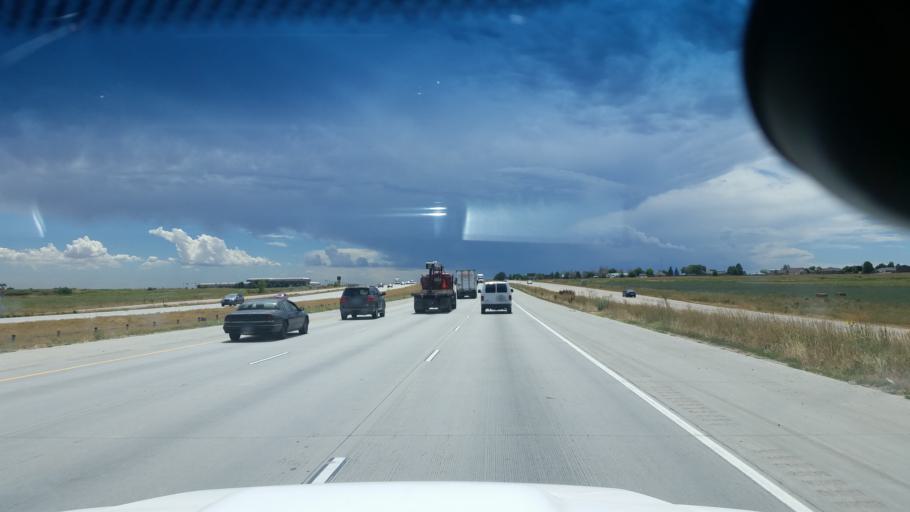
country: US
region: Colorado
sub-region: Weld County
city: Firestone
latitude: 40.1298
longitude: -104.9806
